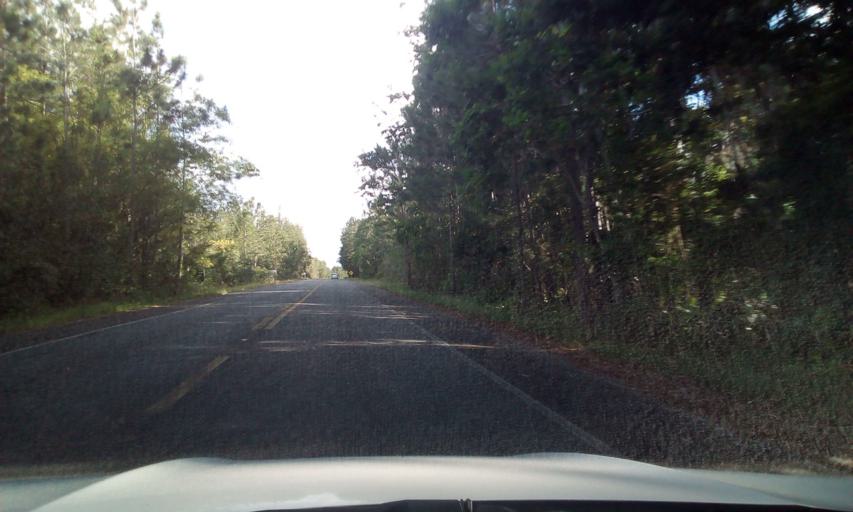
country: BR
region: Bahia
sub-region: Conde
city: Conde
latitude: -12.1074
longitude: -37.7840
